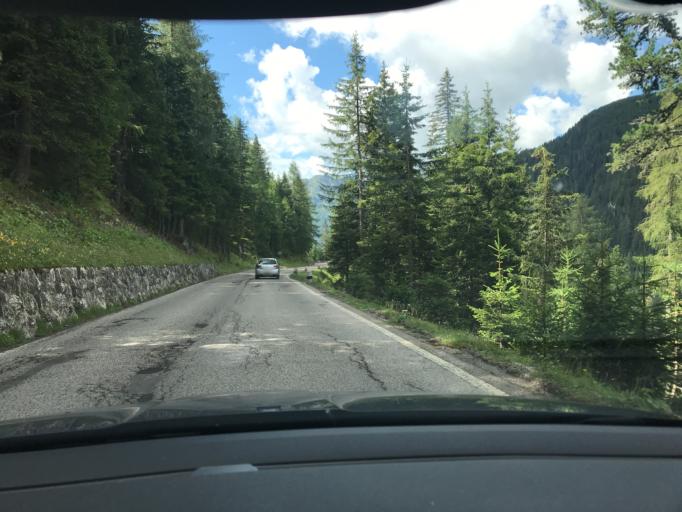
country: IT
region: Veneto
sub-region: Provincia di Belluno
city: Livinallongo del Col di Lana
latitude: 46.5013
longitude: 11.9937
